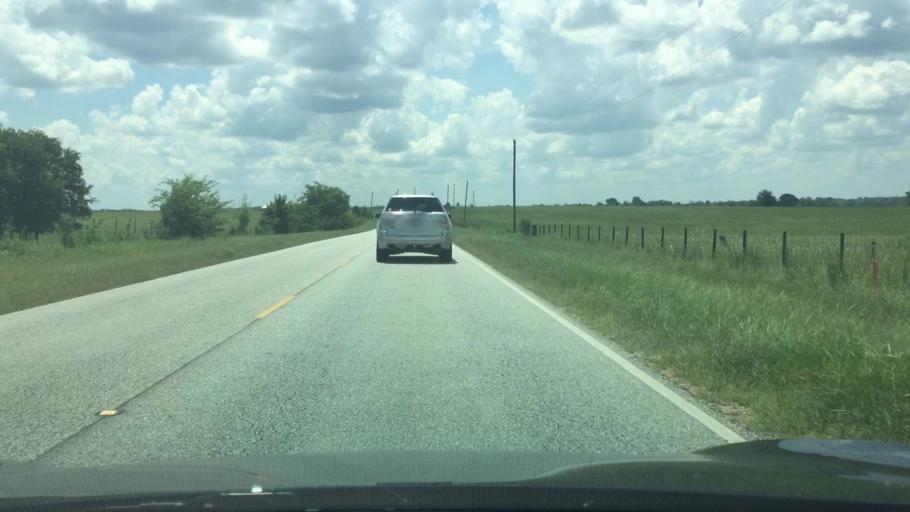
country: US
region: Alabama
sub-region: Montgomery County
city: Pike Road
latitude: 32.2766
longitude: -86.1011
